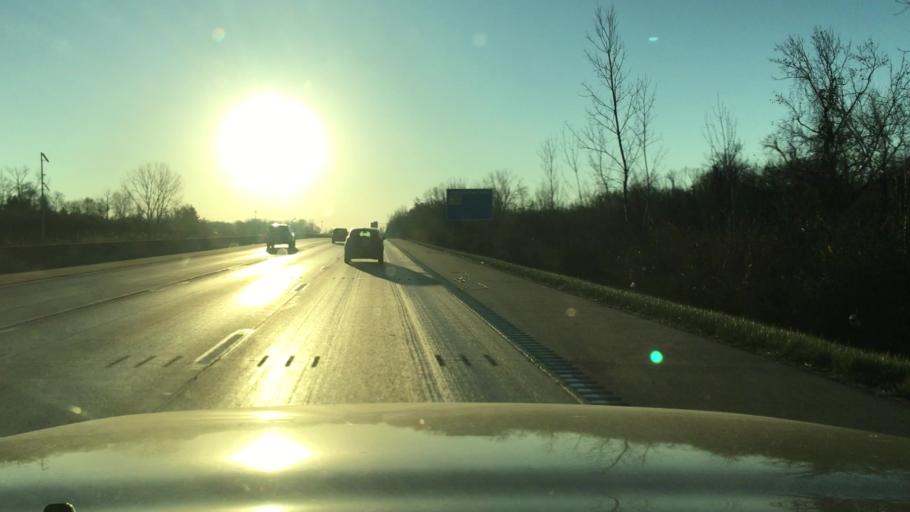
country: US
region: Missouri
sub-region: Saint Charles County
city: Saint Charles
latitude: 38.8167
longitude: -90.4953
